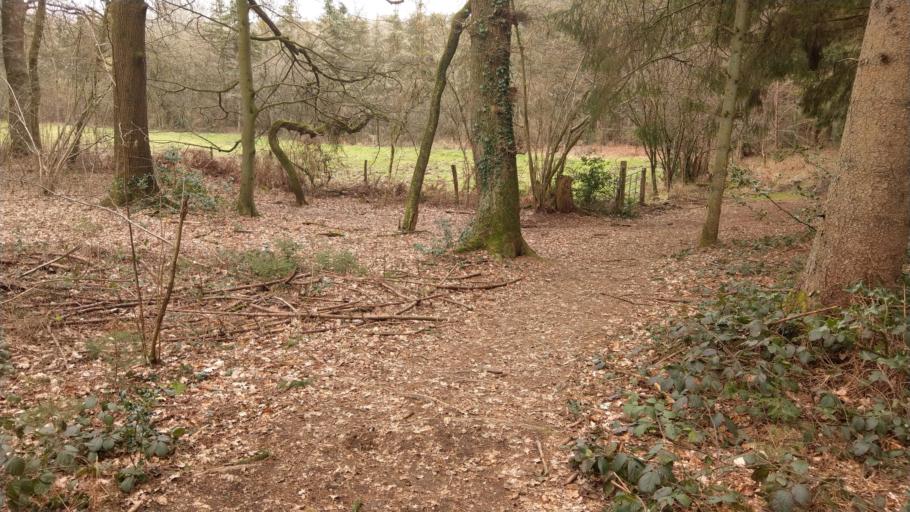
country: BE
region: Wallonia
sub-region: Province de Liege
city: La Calamine
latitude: 50.7285
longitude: 6.0285
